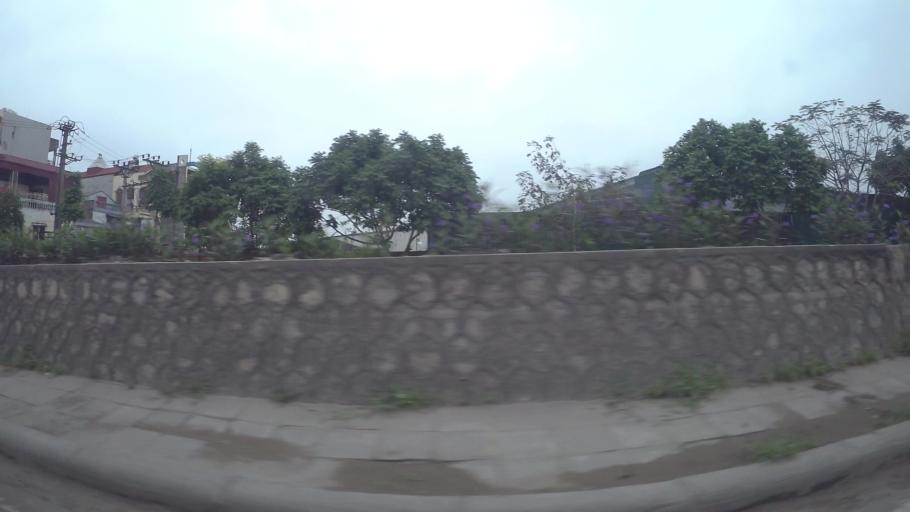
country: VN
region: Ha Noi
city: Hai BaTrung
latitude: 21.0009
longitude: 105.8804
